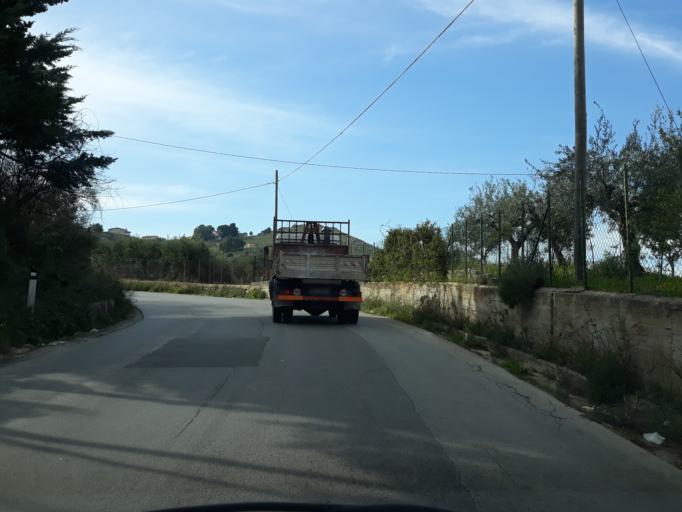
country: IT
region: Sicily
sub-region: Palermo
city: Piano Maglio-Blandino
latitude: 38.0408
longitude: 13.3166
